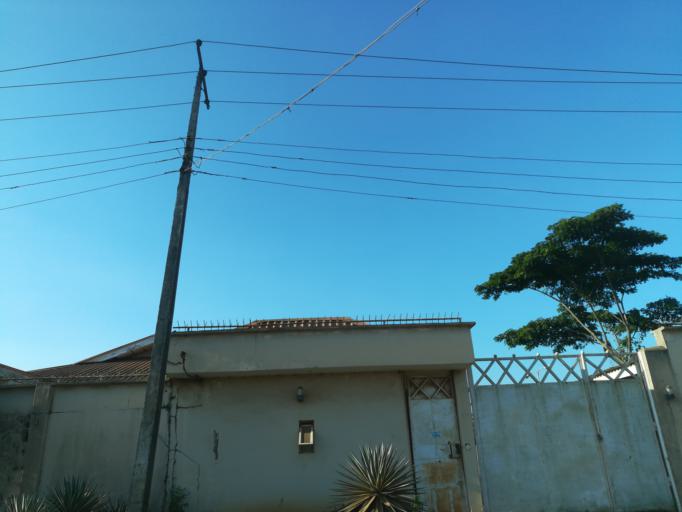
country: NG
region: Lagos
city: Ikorodu
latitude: 6.5819
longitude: 3.5281
